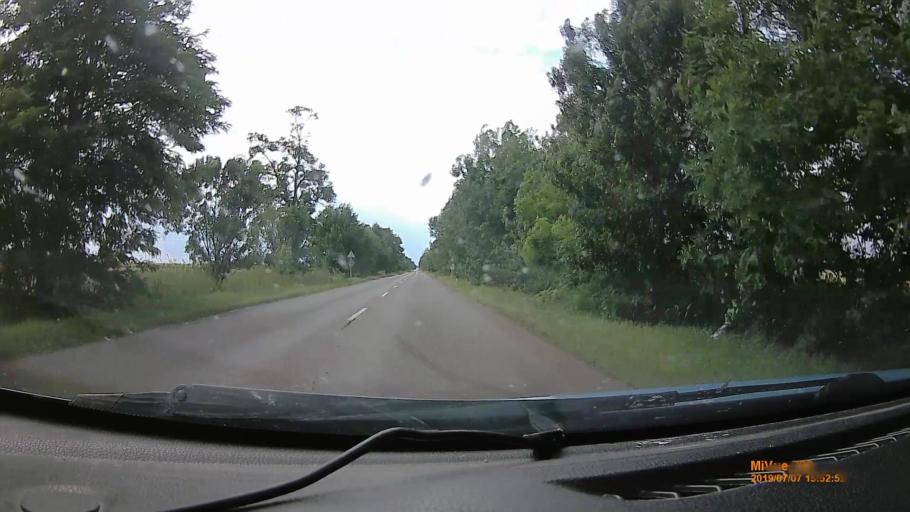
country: HU
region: Pest
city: Szentlorinckata
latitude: 47.5445
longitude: 19.8157
